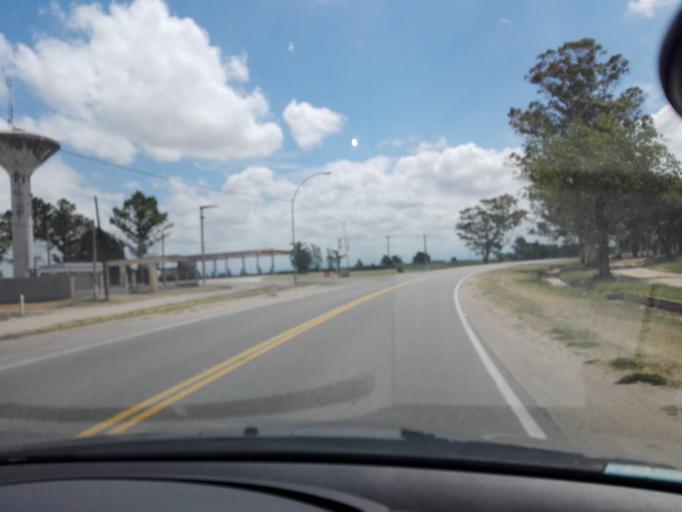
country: AR
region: Cordoba
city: Toledo
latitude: -31.6504
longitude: -64.0905
